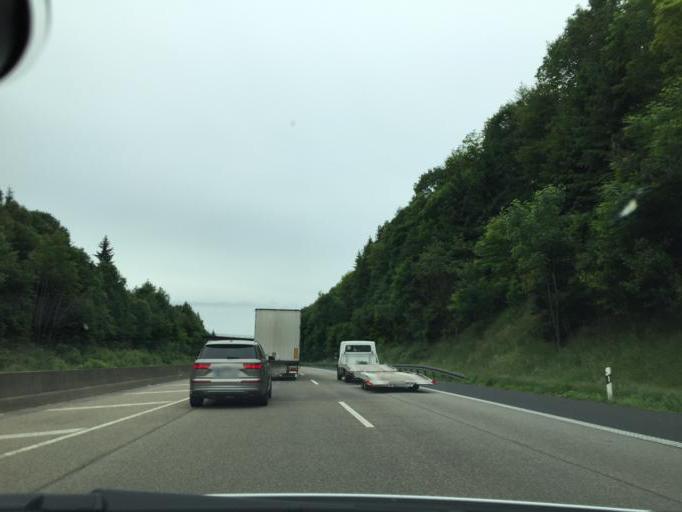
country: DE
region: Bavaria
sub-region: Regierungsbezirk Unterfranken
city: Motten
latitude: 50.3689
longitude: 9.7324
